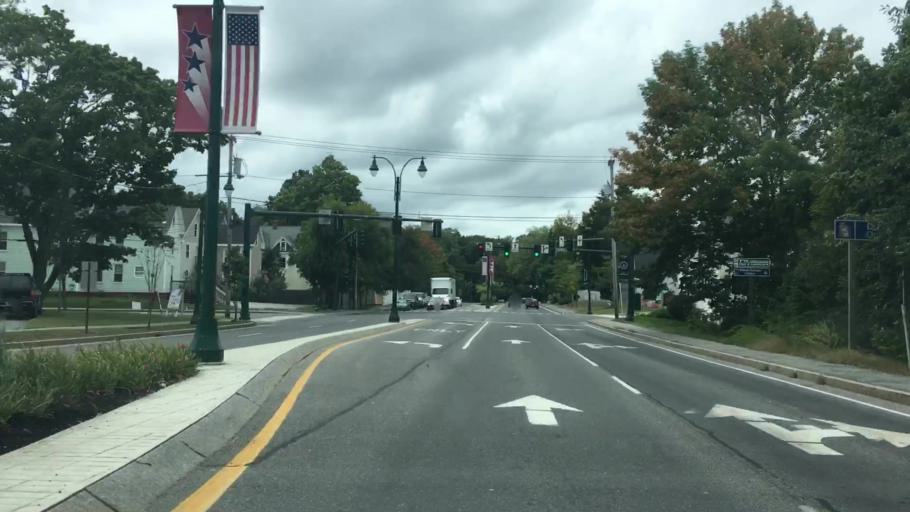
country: US
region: Maine
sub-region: Cumberland County
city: Westbrook
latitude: 43.6766
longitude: -70.3595
